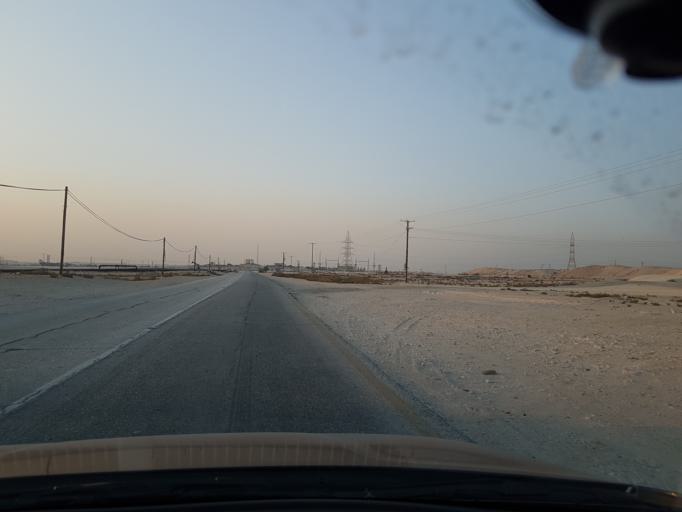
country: BH
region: Central Governorate
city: Dar Kulayb
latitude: 26.0656
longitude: 50.5533
